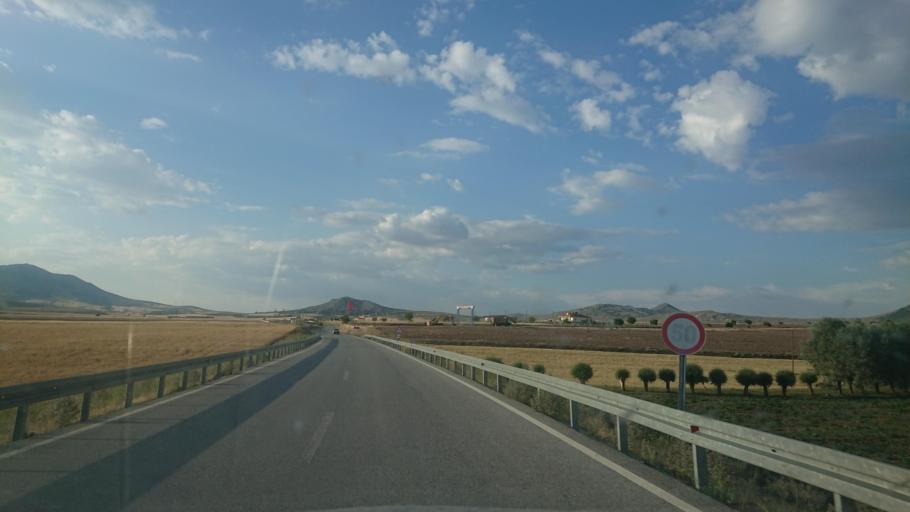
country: TR
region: Aksaray
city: Balci
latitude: 38.5566
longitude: 34.1044
